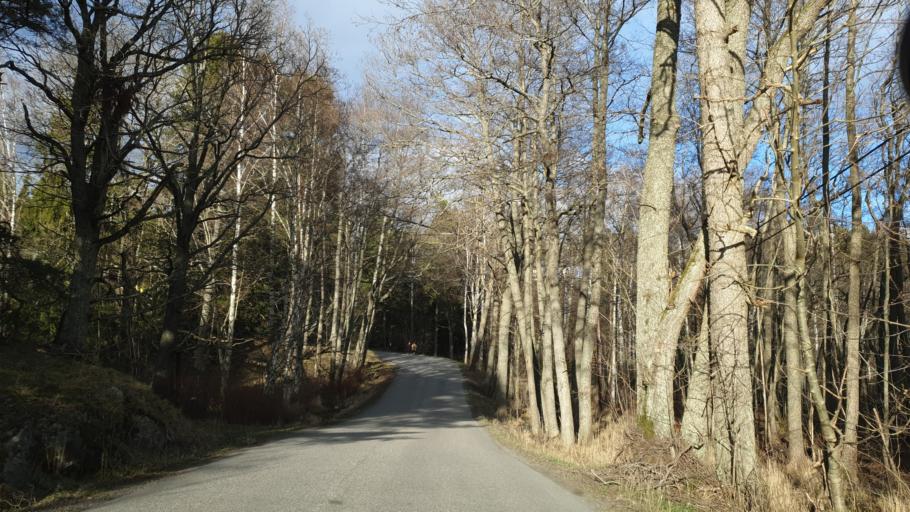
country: SE
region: Stockholm
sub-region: Varmdo Kommun
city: Holo
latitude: 59.3595
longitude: 18.6687
